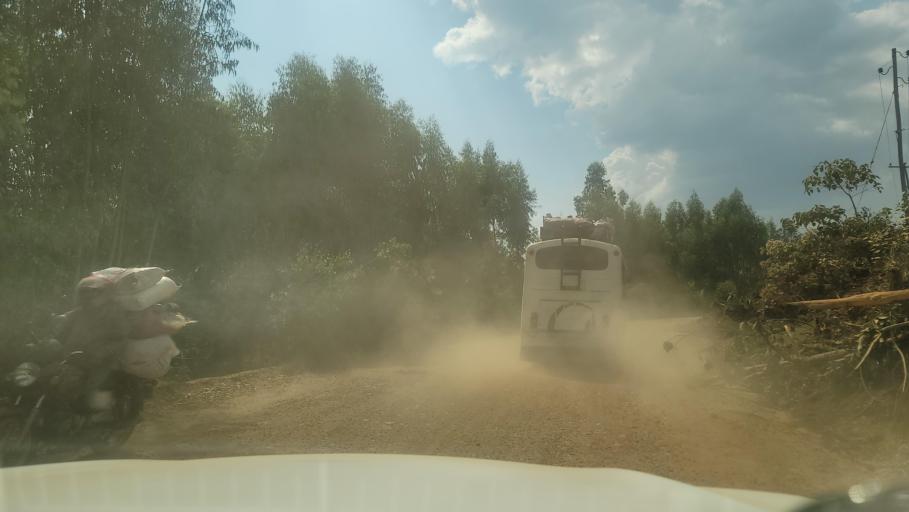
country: ET
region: Oromiya
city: Agaro
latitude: 7.8137
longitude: 36.5114
